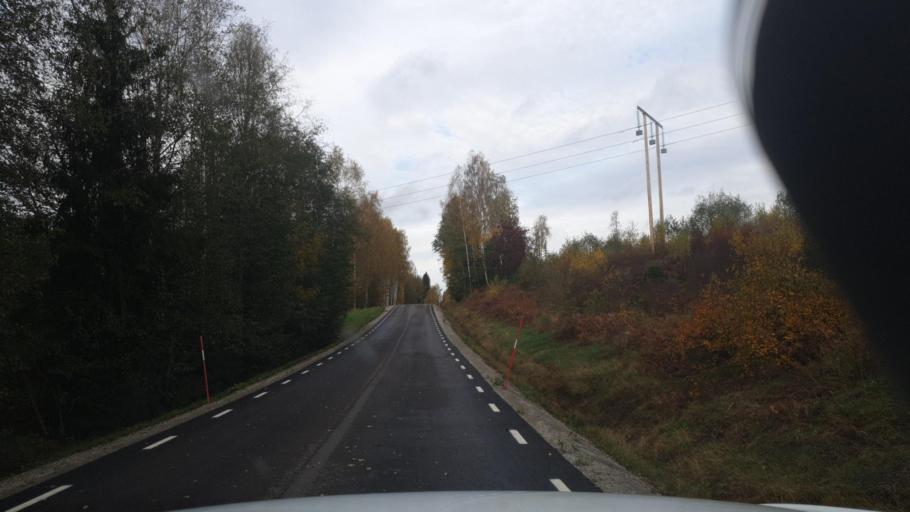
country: SE
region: Vaermland
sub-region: Sunne Kommun
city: Sunne
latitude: 59.6724
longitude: 12.9043
